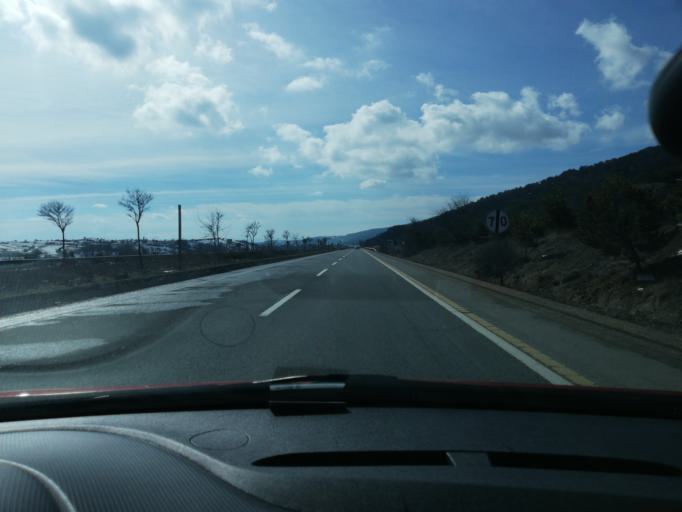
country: TR
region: Karabuk
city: Gozyeri
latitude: 40.8495
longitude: 32.4587
